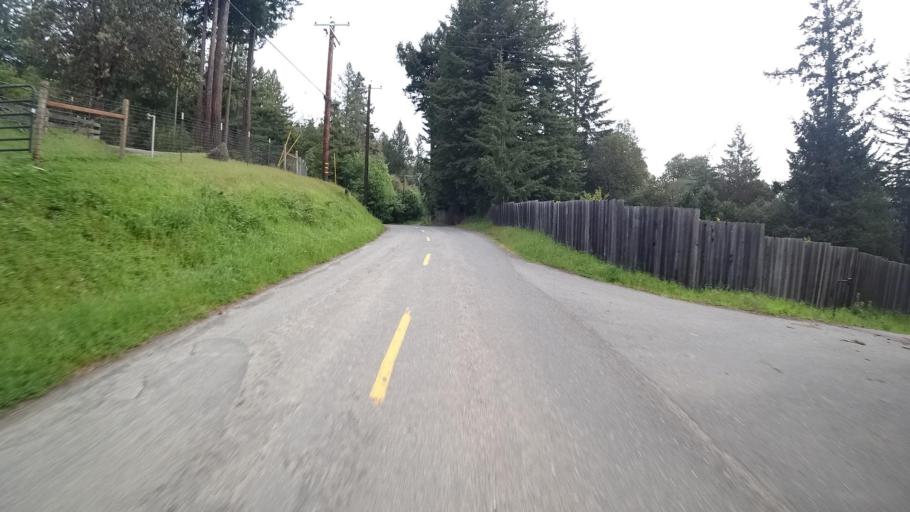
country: US
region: California
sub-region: Humboldt County
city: Redway
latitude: 40.3040
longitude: -123.8213
